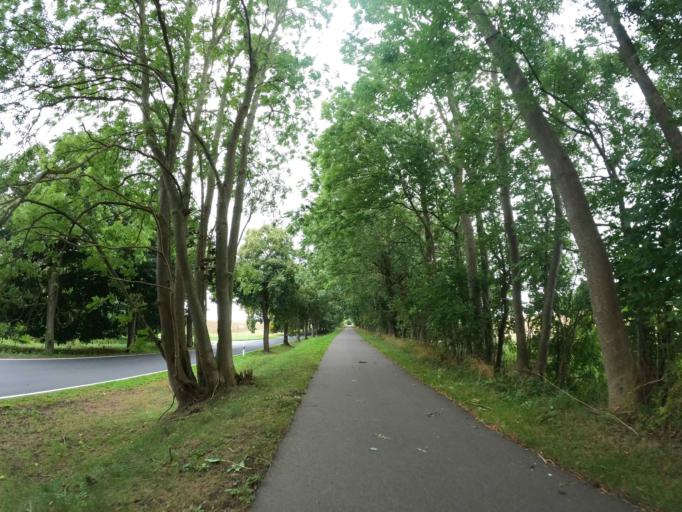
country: DE
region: Mecklenburg-Vorpommern
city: Poseritz
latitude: 54.2888
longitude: 13.3092
